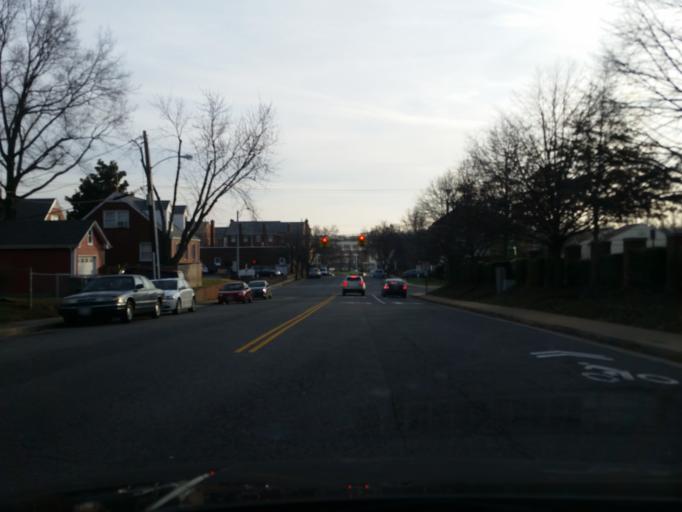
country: US
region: Virginia
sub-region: Fairfax County
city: Huntington
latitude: 38.8274
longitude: -77.0848
